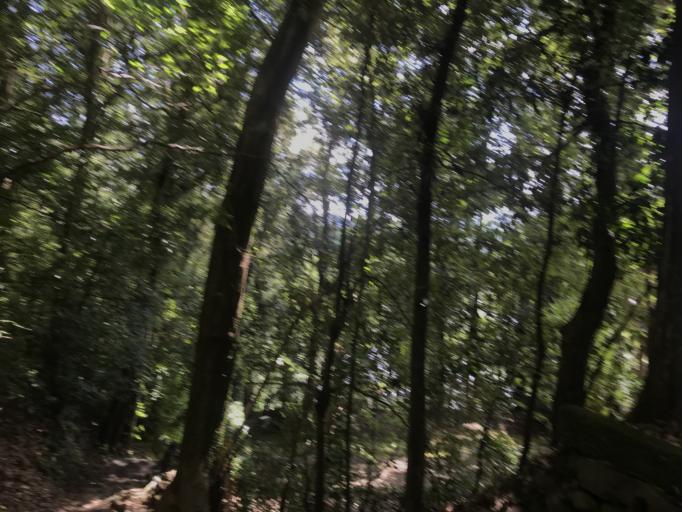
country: JP
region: Wakayama
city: Shingu
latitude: 33.8397
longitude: 135.7741
